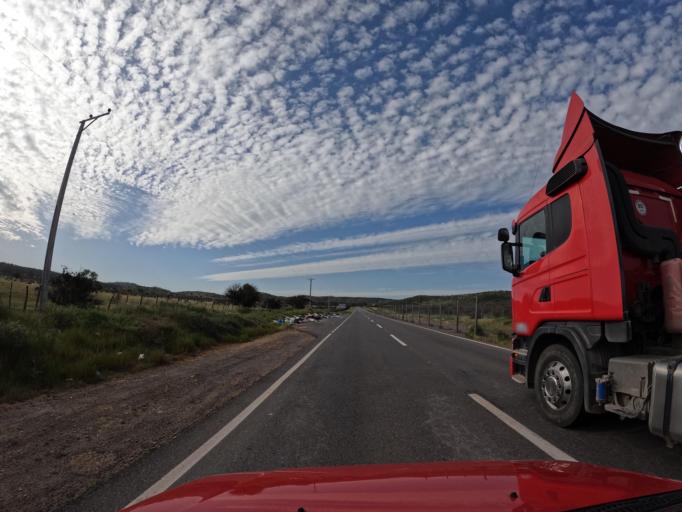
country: CL
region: O'Higgins
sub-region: Provincia de Colchagua
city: Santa Cruz
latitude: -34.3247
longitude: -71.7437
